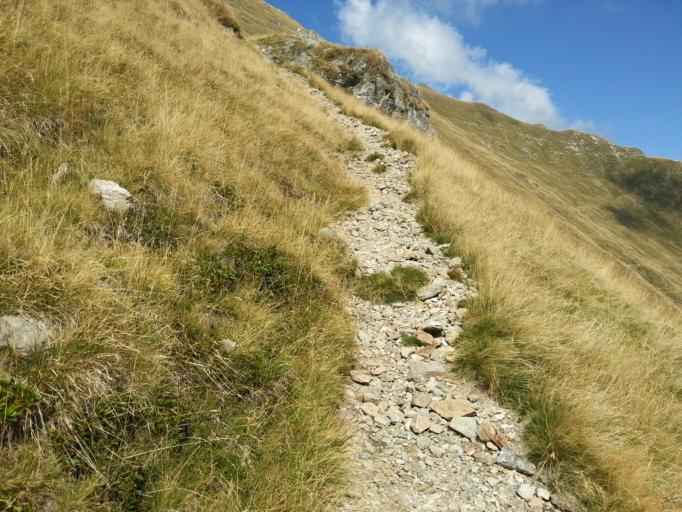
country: CH
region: Grisons
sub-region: Moesa District
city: Roveredo
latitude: 46.1671
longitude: 9.1725
